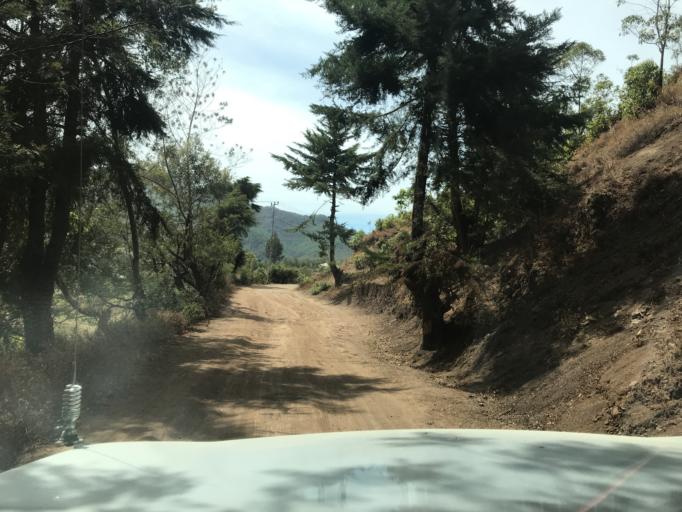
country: TL
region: Ainaro
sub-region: Ainaro
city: Ainaro
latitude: -8.8912
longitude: 125.5176
